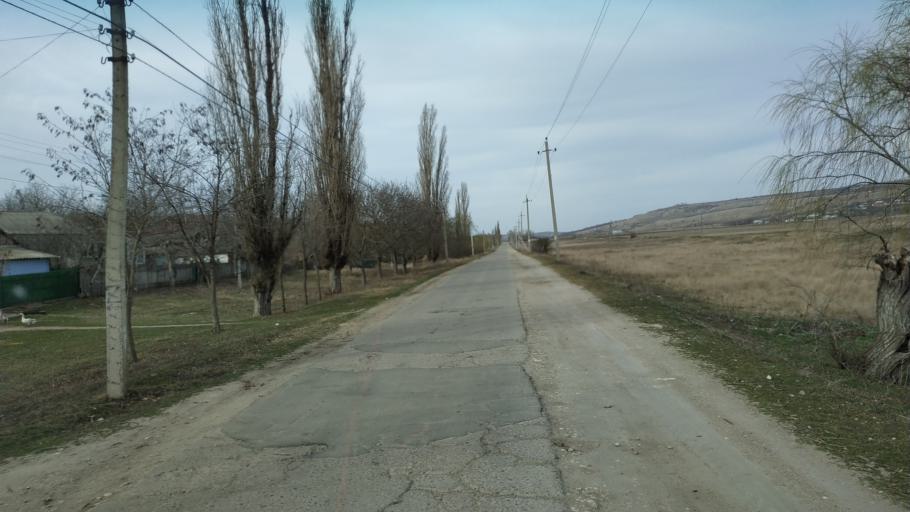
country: RO
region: Vaslui
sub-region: Comuna Dranceni
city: Dranceni
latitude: 46.8651
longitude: 28.2006
